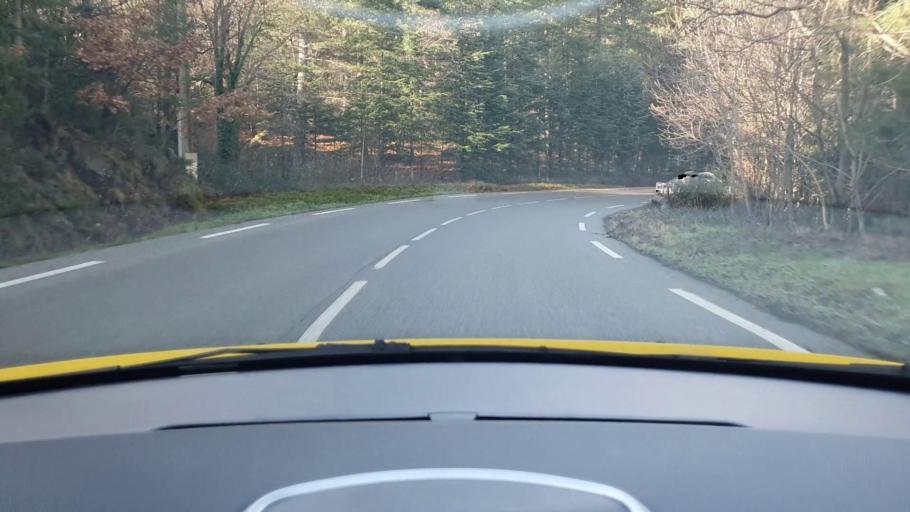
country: FR
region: Languedoc-Roussillon
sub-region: Departement du Gard
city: Branoux-les-Taillades
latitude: 44.3743
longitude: 3.9417
